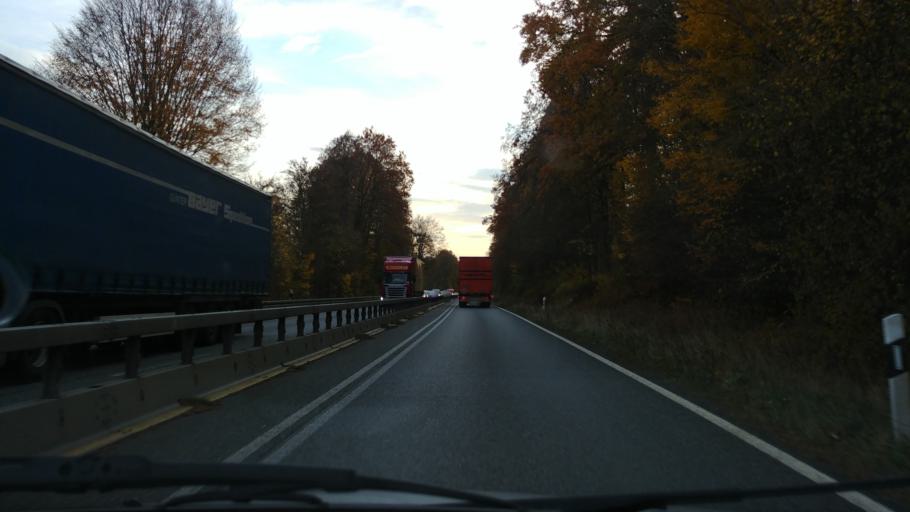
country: DE
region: Hesse
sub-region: Regierungsbezirk Giessen
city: Lohnberg
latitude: 50.5231
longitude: 8.2764
